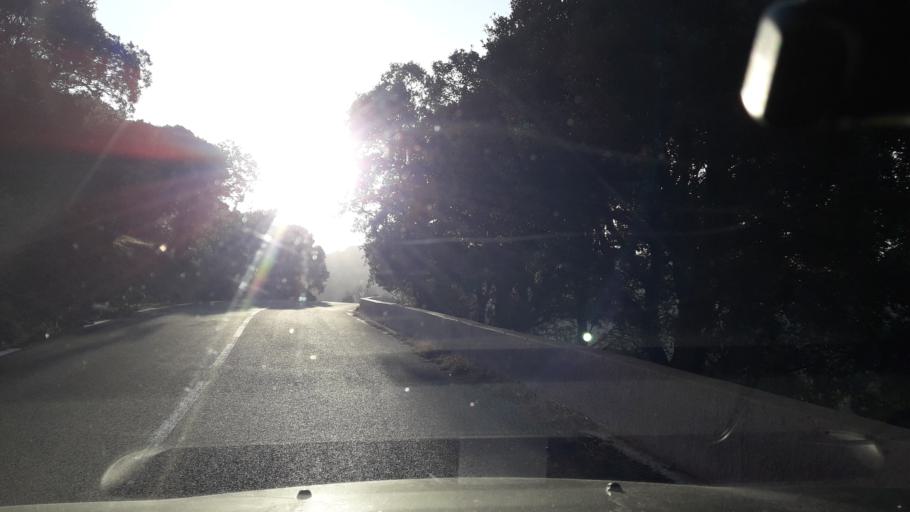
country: FR
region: Provence-Alpes-Cote d'Azur
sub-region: Departement du Var
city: Tanneron
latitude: 43.5160
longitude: 6.8190
